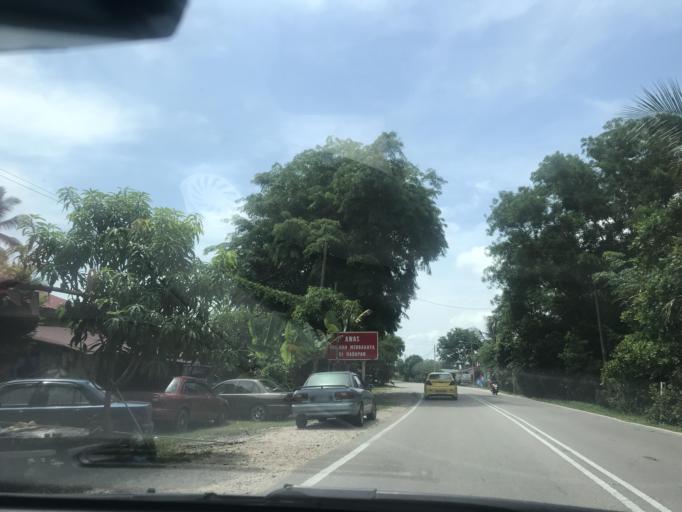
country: MY
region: Kelantan
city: Tumpat
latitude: 6.2055
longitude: 102.1480
